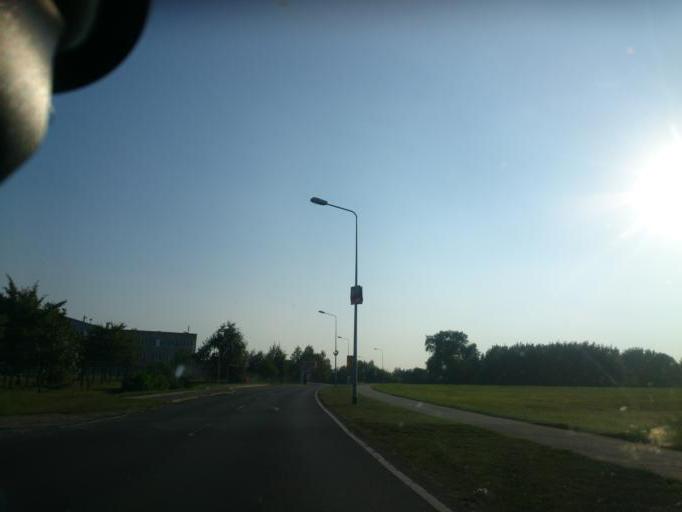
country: DE
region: Mecklenburg-Vorpommern
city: Lambrechtshagen
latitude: 54.1119
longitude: 12.0525
